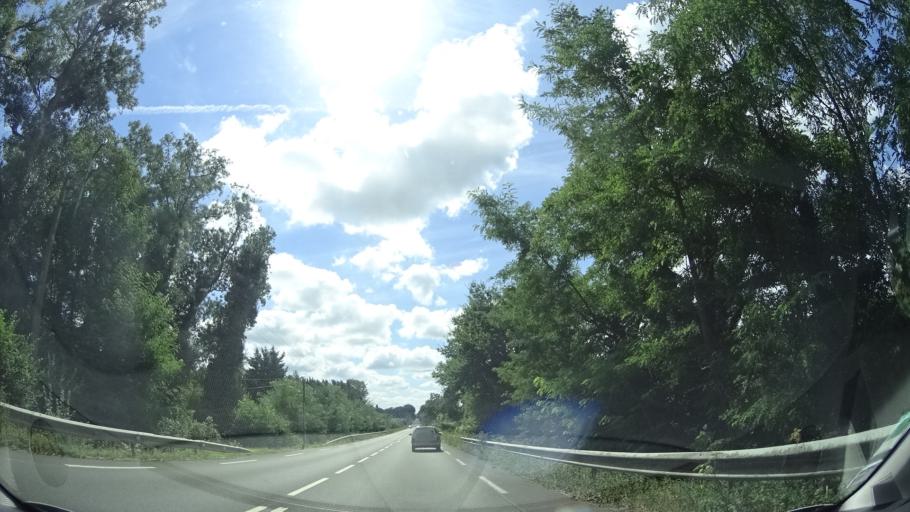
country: FR
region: Pays de la Loire
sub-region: Departement de la Sarthe
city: La Fleche
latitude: 47.7246
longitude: -0.1108
